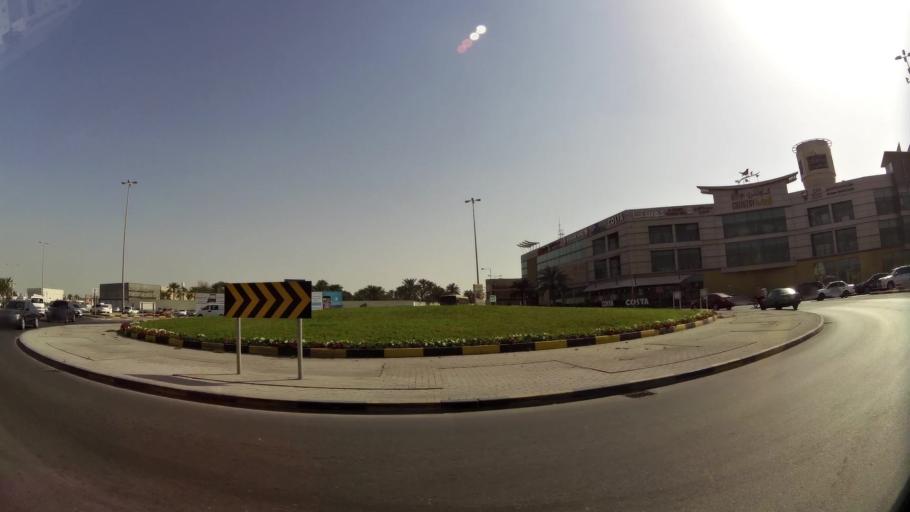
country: BH
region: Manama
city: Jidd Hafs
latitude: 26.2199
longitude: 50.5108
